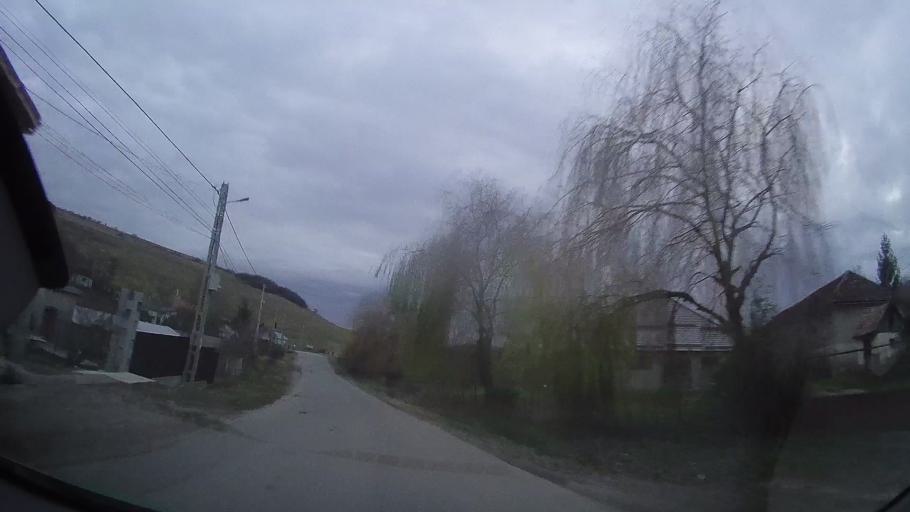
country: RO
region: Cluj
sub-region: Comuna Caianu
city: Vaida-Camaras
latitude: 46.8223
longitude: 23.9386
